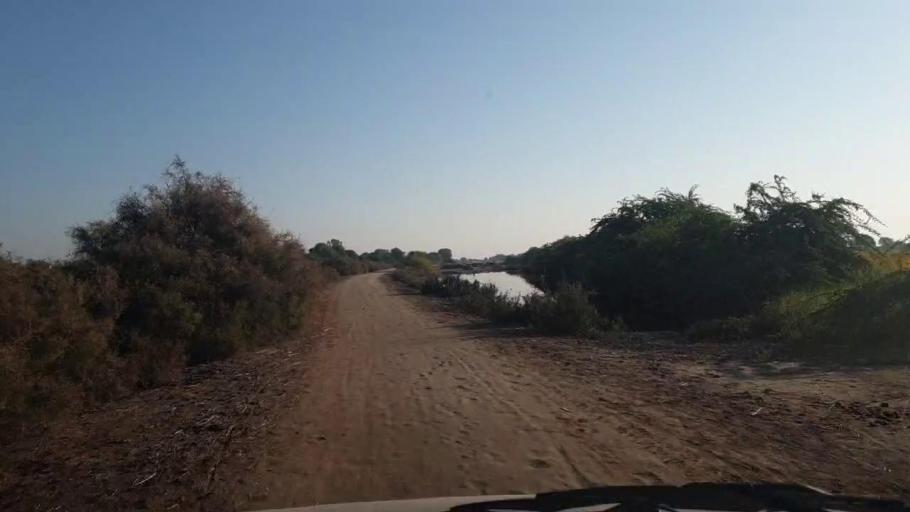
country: PK
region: Sindh
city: Talhar
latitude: 24.8032
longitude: 68.8227
